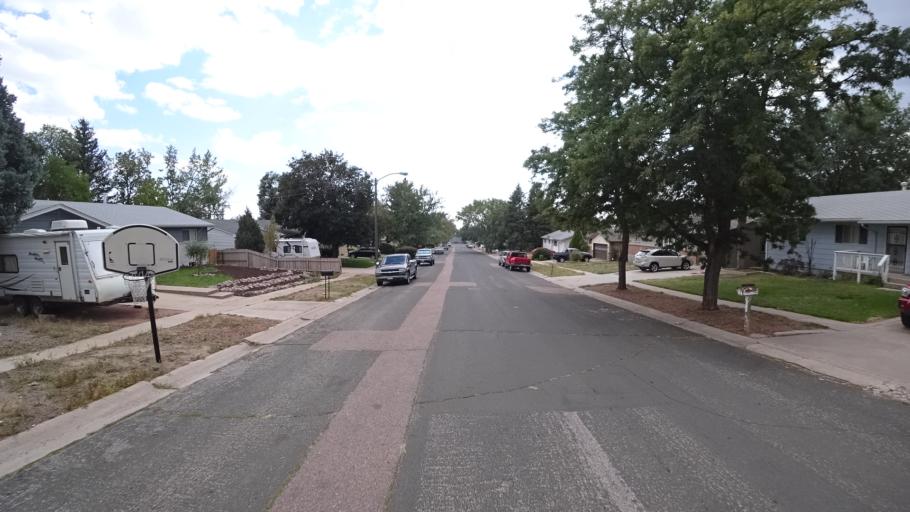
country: US
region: Colorado
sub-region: El Paso County
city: Cimarron Hills
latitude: 38.8531
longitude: -104.7594
